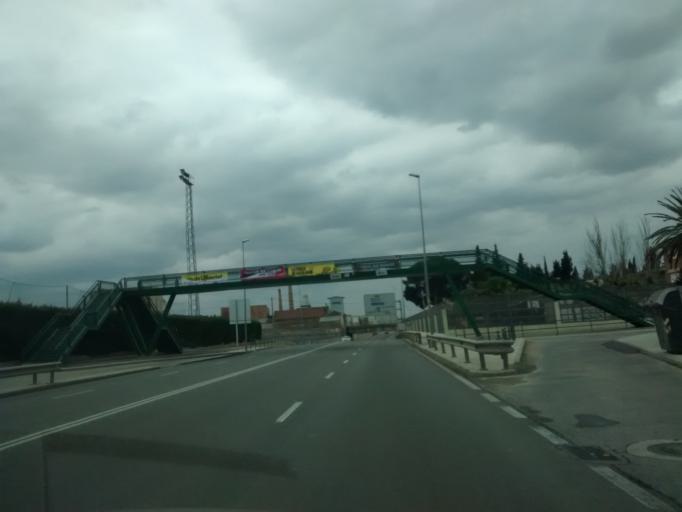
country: ES
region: Catalonia
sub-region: Provincia de Tarragona
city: Tortosa
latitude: 40.8138
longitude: 0.5119
